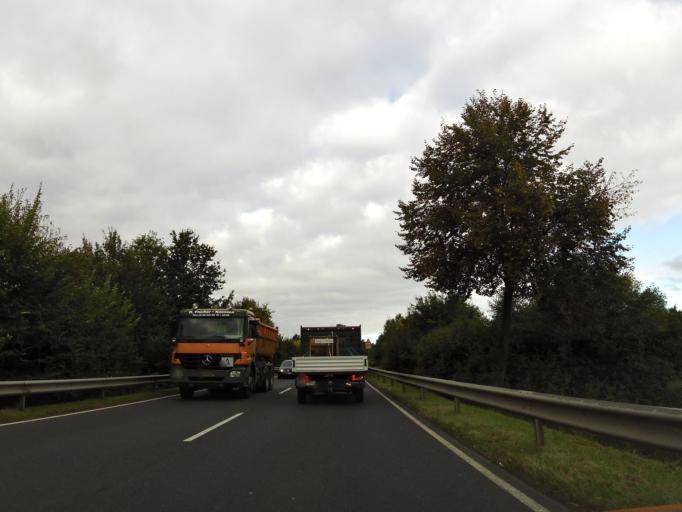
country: DE
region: Lower Saxony
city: Einbeck
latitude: 51.8073
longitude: 9.8480
